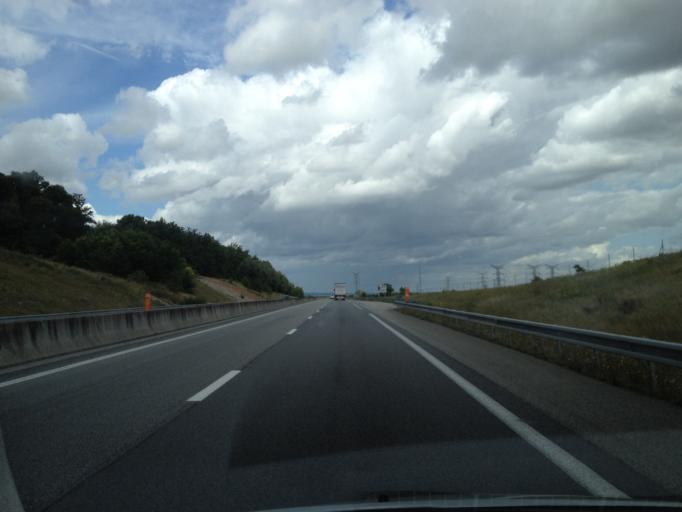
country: FR
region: Pays de la Loire
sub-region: Departement de la Sarthe
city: Arconnay
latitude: 48.3719
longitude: 0.1027
